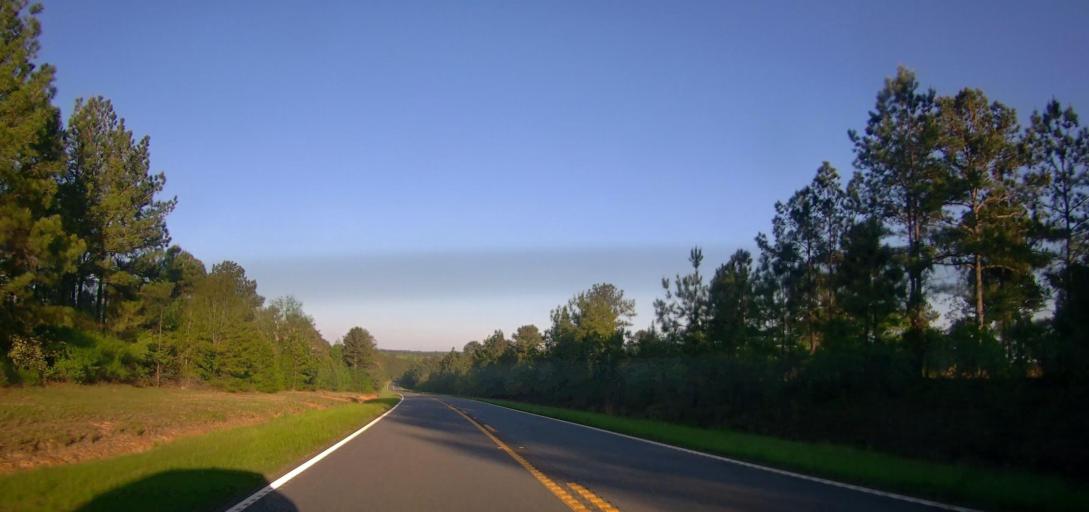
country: US
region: Georgia
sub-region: Marion County
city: Buena Vista
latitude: 32.3625
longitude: -84.4020
